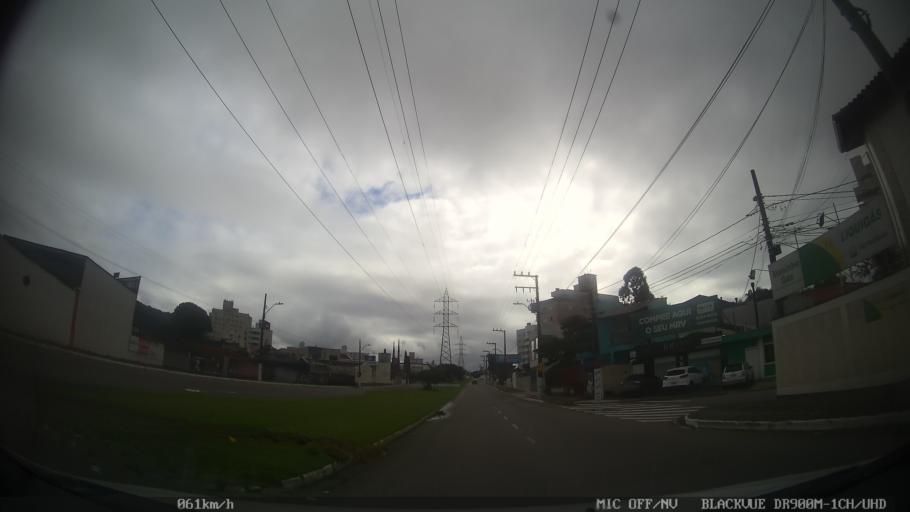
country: BR
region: Santa Catarina
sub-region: Sao Jose
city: Campinas
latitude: -27.5818
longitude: -48.6209
